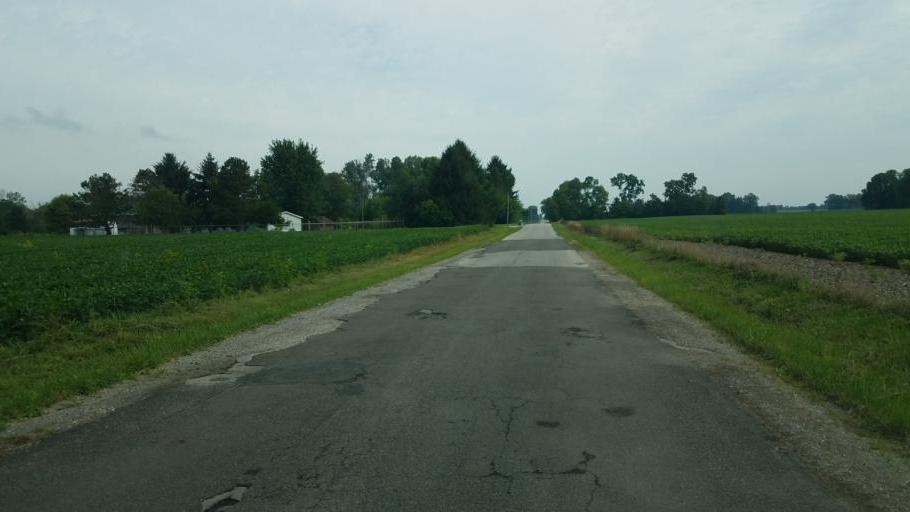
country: US
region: Ohio
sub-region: Delaware County
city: Ashley
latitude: 40.4411
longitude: -82.9064
